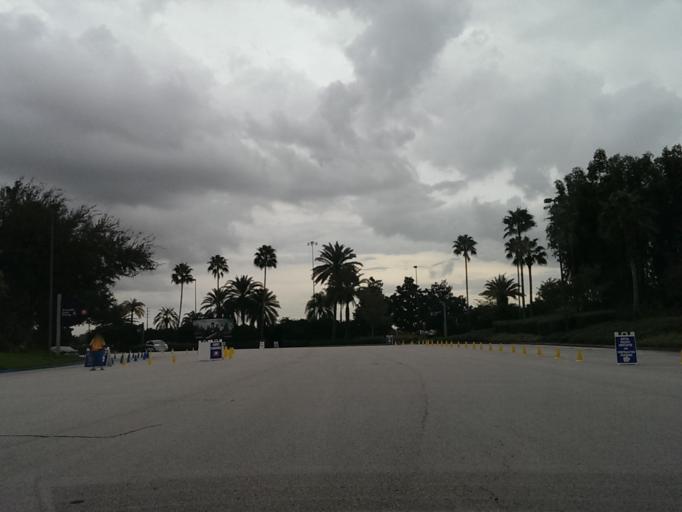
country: US
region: Florida
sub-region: Orange County
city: Tangelo Park
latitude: 28.4738
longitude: -81.4609
